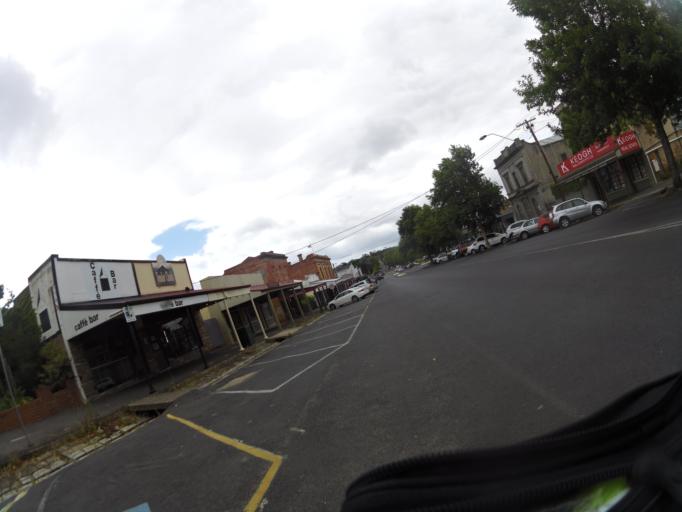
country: AU
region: Victoria
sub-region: Mount Alexander
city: Castlemaine
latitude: -37.0650
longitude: 144.2196
